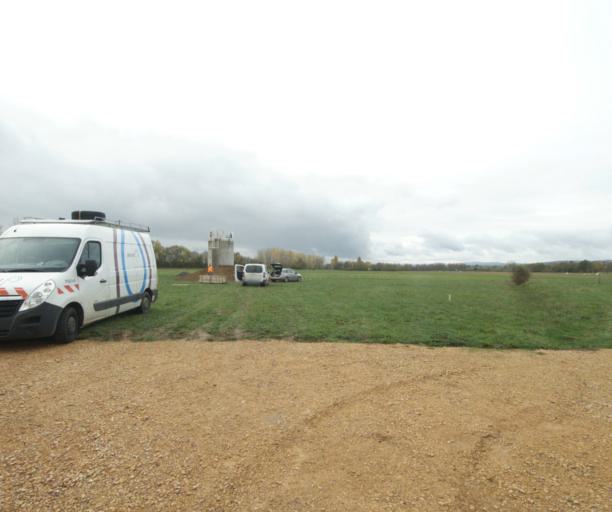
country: FR
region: Rhone-Alpes
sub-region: Departement de l'Ain
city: Pont-de-Vaux
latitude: 46.4556
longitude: 4.9006
